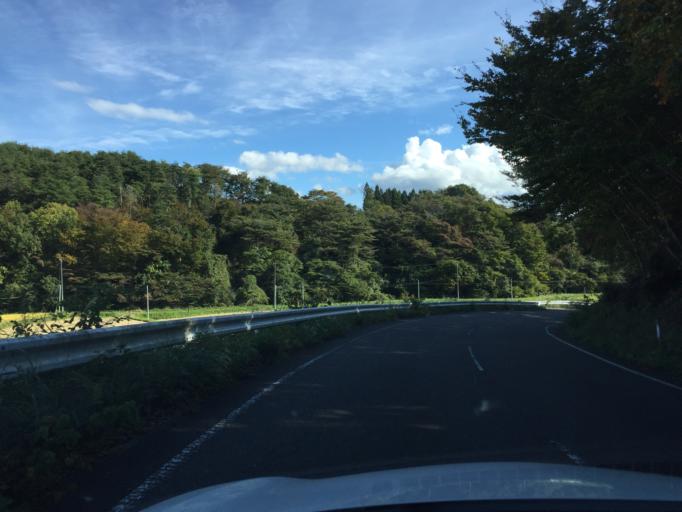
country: JP
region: Fukushima
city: Ishikawa
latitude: 37.1507
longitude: 140.5958
